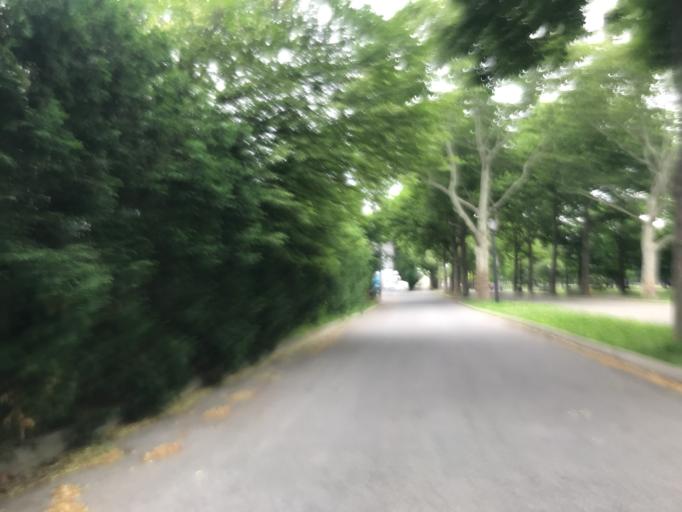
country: US
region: New York
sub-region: Queens County
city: Borough of Queens
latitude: 40.7488
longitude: -73.8442
